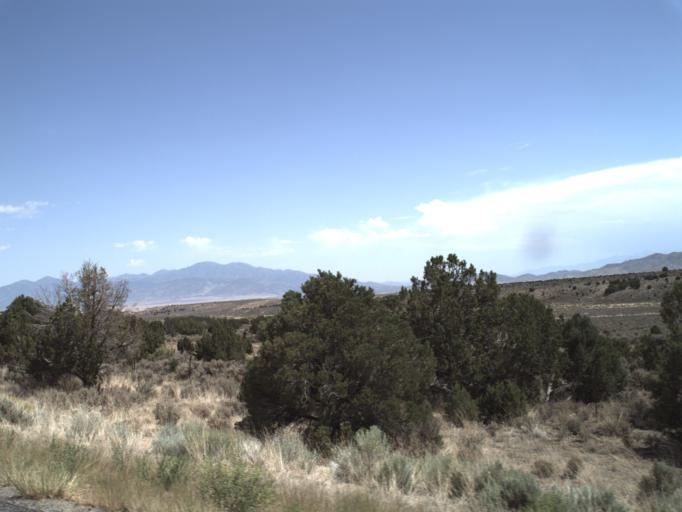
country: US
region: Utah
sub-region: Utah County
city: Eagle Mountain
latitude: 40.0293
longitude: -112.2833
